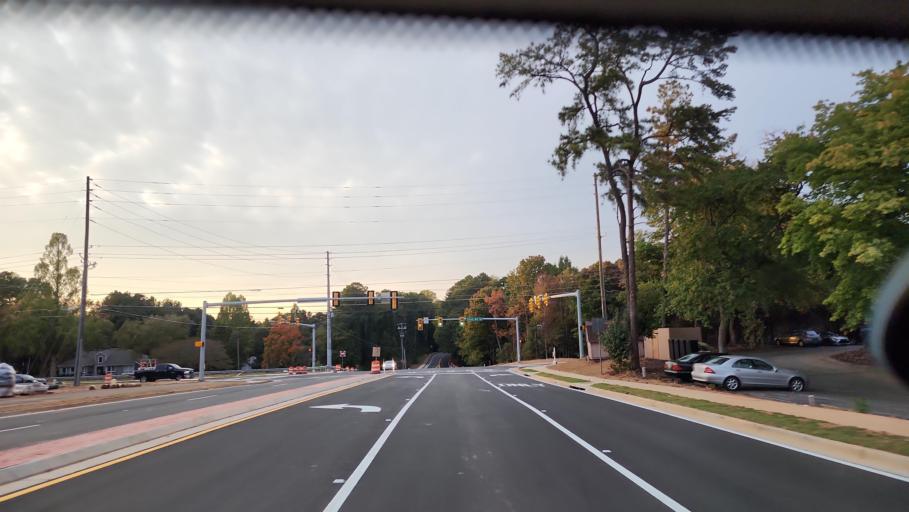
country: US
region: Georgia
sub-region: Cobb County
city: Vinings
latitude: 33.9133
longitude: -84.4710
